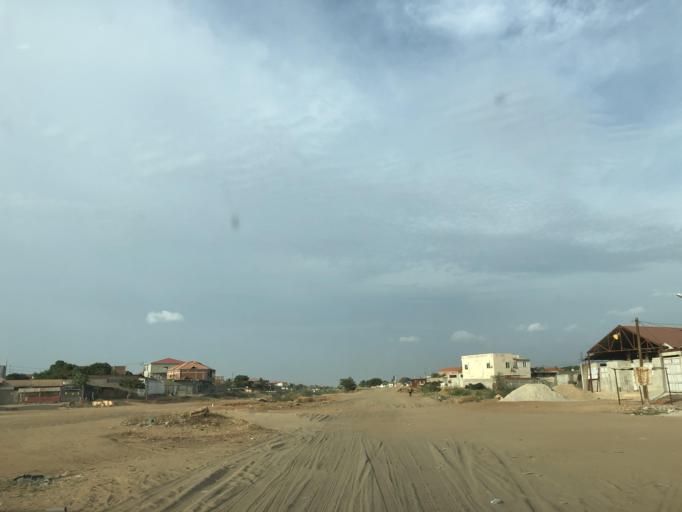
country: AO
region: Luanda
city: Luanda
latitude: -8.9247
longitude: 13.3057
